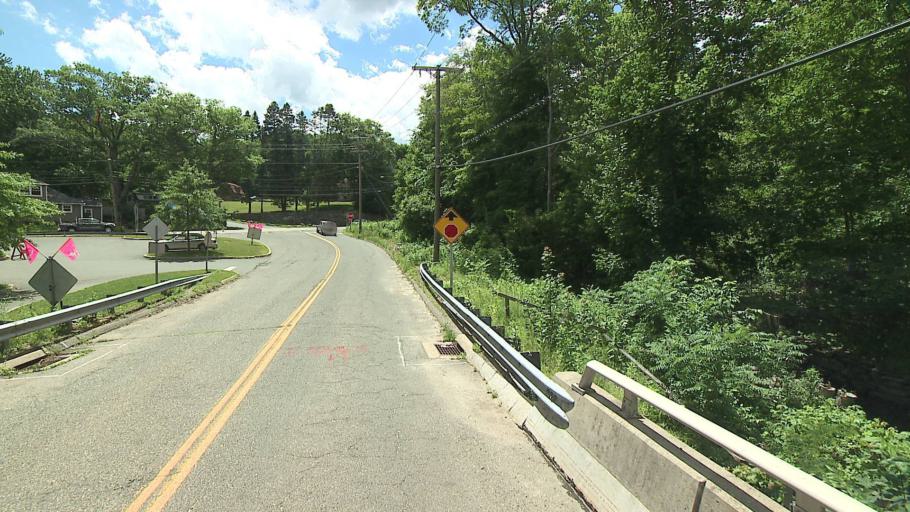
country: US
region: Connecticut
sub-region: Litchfield County
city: New Preston
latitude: 41.6826
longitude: -73.3538
